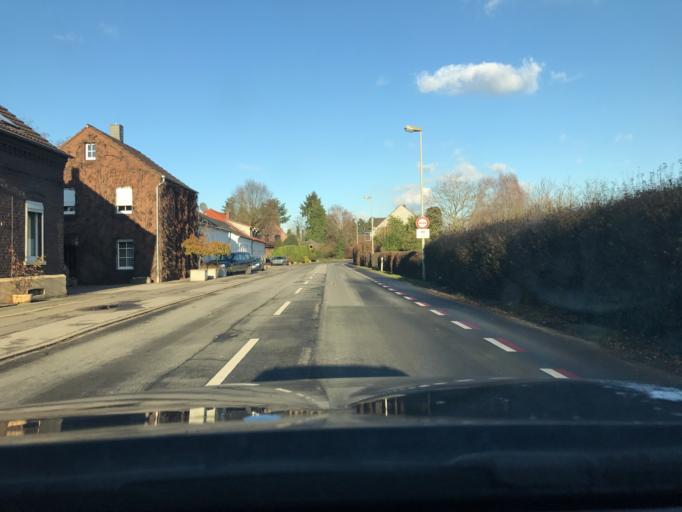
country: DE
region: North Rhine-Westphalia
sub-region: Regierungsbezirk Dusseldorf
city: Krefeld
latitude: 51.3675
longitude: 6.5725
